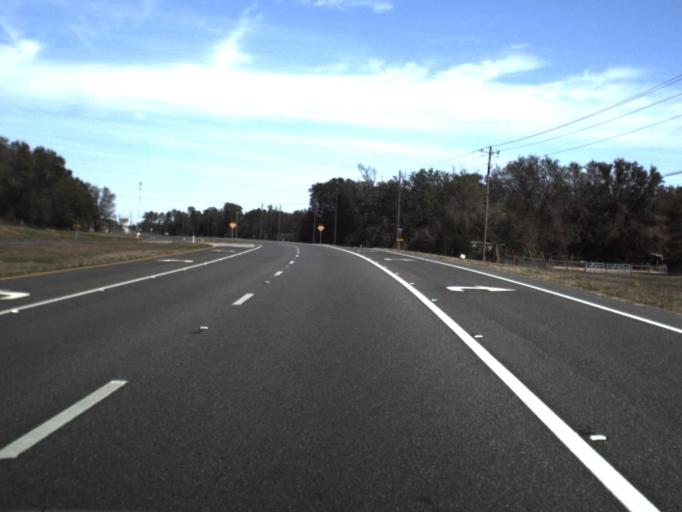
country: US
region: Florida
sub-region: Bay County
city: Lynn Haven
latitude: 30.4235
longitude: -85.6881
